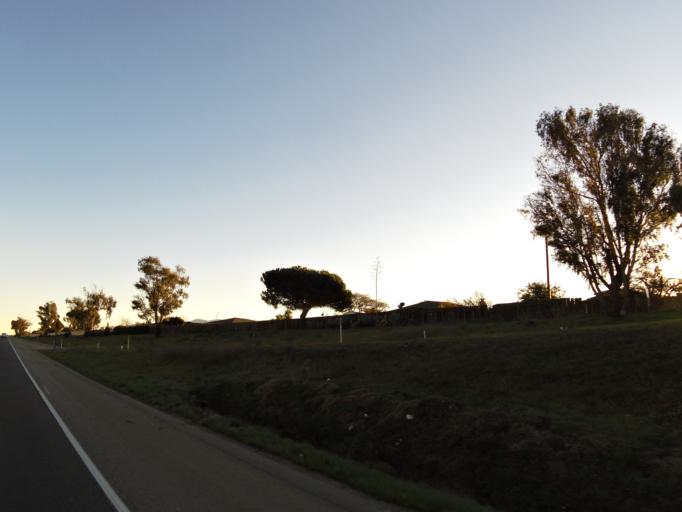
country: US
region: California
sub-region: Monterey County
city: Gonzales
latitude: 36.5128
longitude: -121.4375
